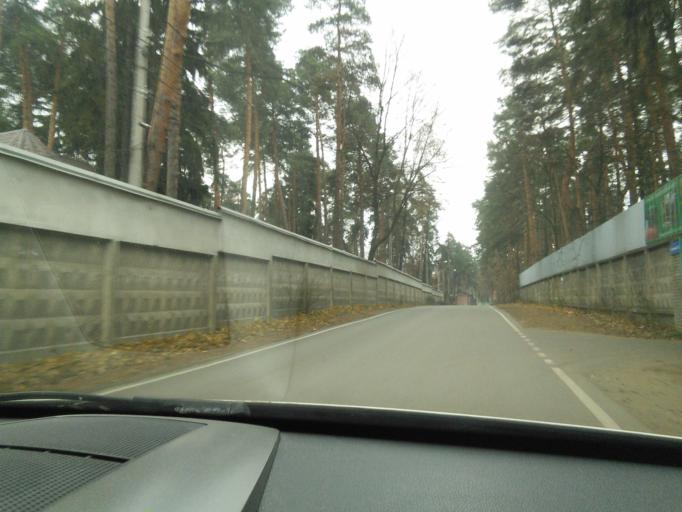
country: RU
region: Moskovskaya
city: Kraskovo
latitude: 55.6409
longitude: 37.9779
